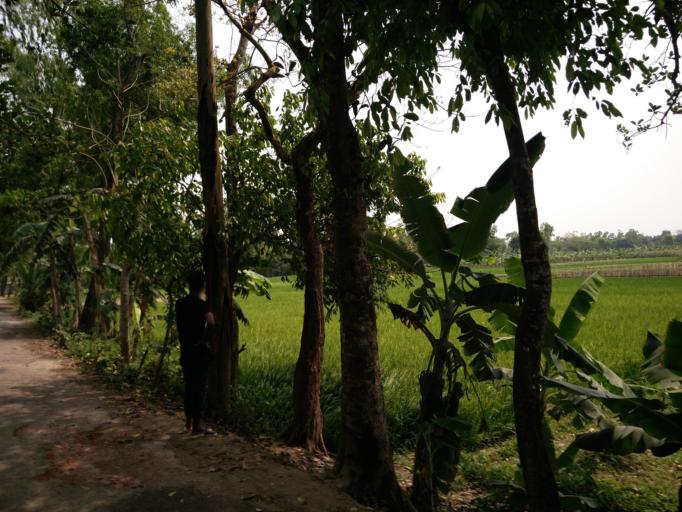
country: BD
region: Dhaka
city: Sherpur
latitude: 24.9336
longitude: 90.1664
